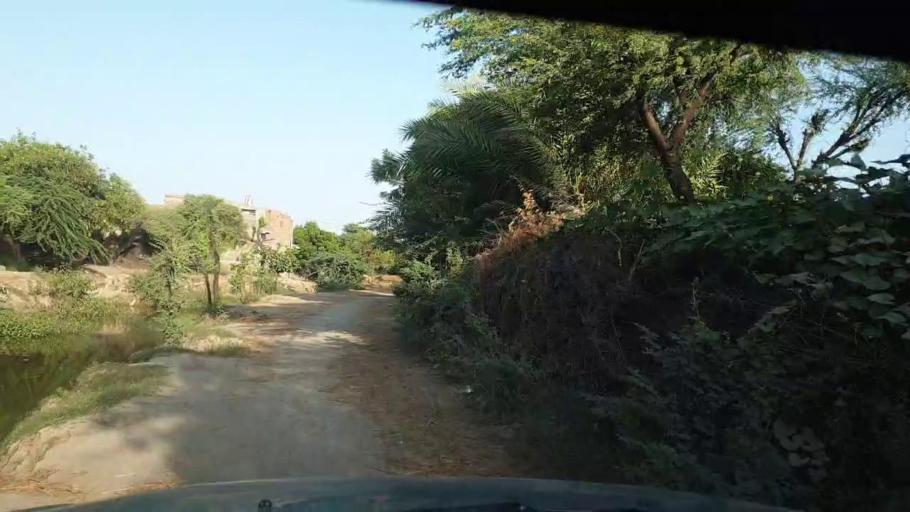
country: PK
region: Sindh
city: Matli
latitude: 25.0113
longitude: 68.7510
